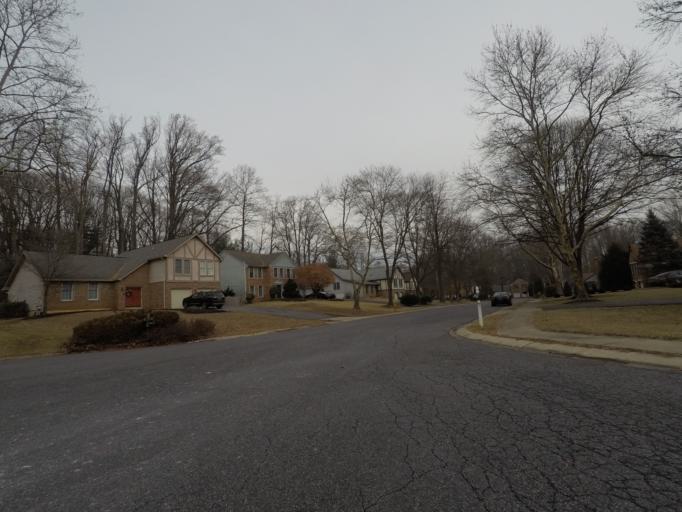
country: US
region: Maryland
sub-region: Howard County
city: Columbia
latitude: 39.2608
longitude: -76.8625
